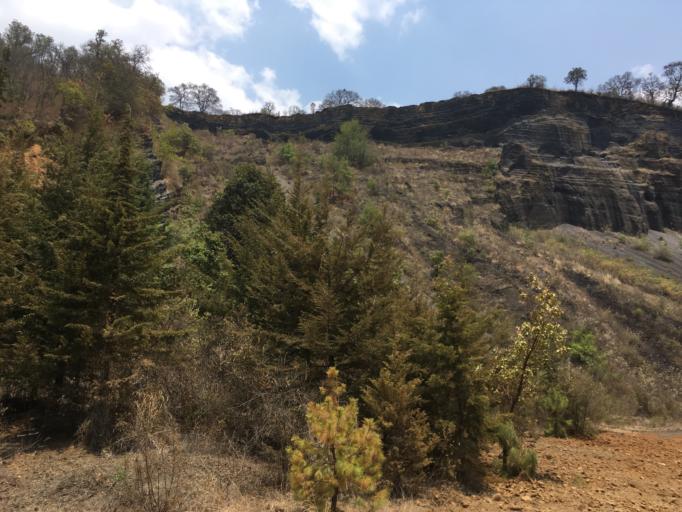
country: MX
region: Michoacan
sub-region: Patzcuaro
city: Santa Ana Chapitiro
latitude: 19.5150
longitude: -101.6432
